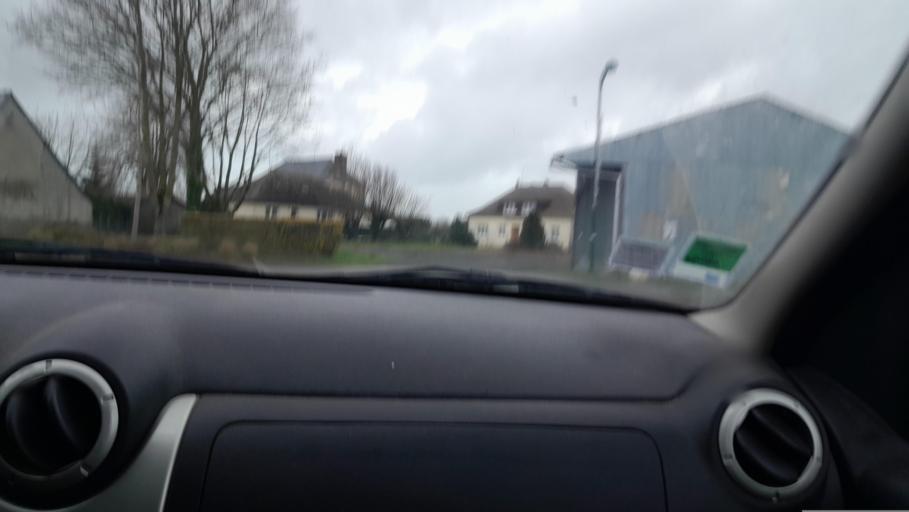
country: FR
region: Brittany
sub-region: Departement d'Ille-et-Vilaine
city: La Guerche-de-Bretagne
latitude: 47.9080
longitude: -1.1409
